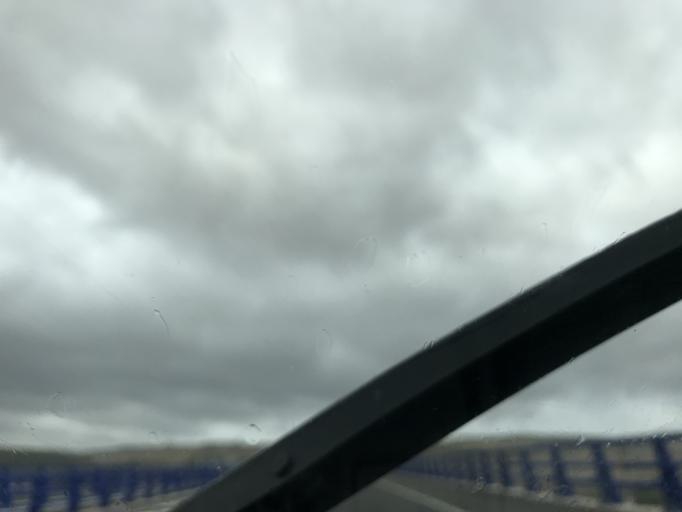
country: ES
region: Andalusia
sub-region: Provincia de Jaen
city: Linares
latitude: 38.0764
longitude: -3.5822
